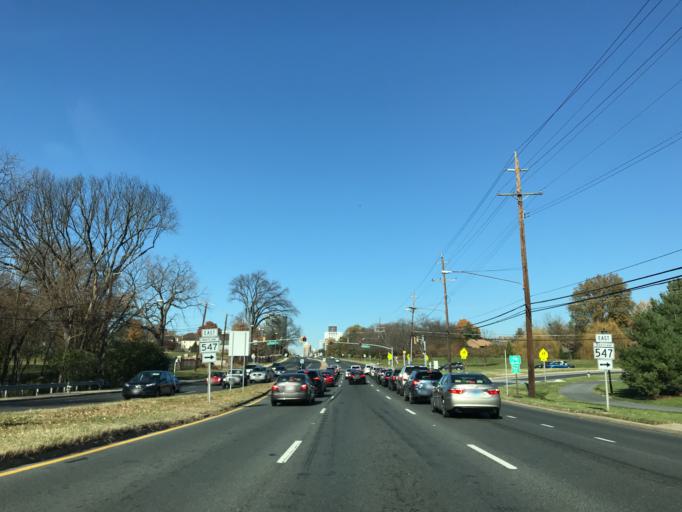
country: US
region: Maryland
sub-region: Montgomery County
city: North Bethesda
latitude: 39.0339
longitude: -77.1065
